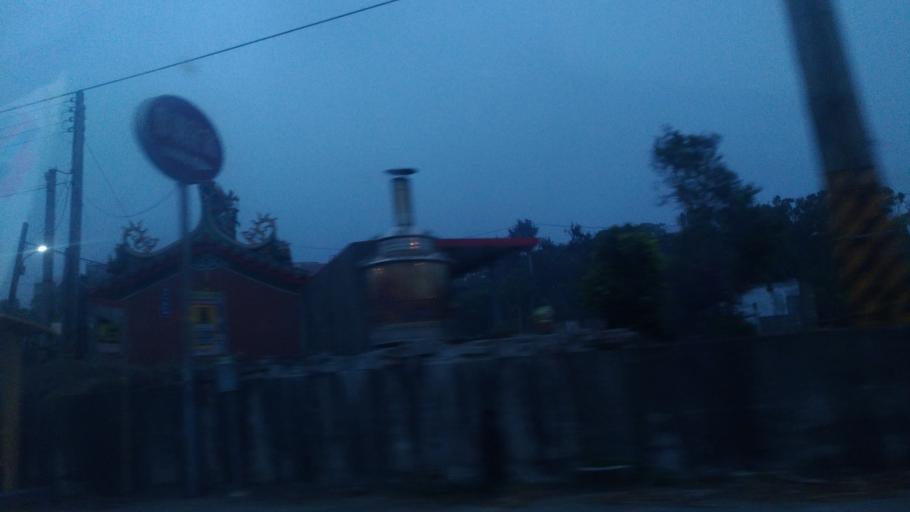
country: TW
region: Taiwan
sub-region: Miaoli
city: Miaoli
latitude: 24.5600
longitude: 120.7072
